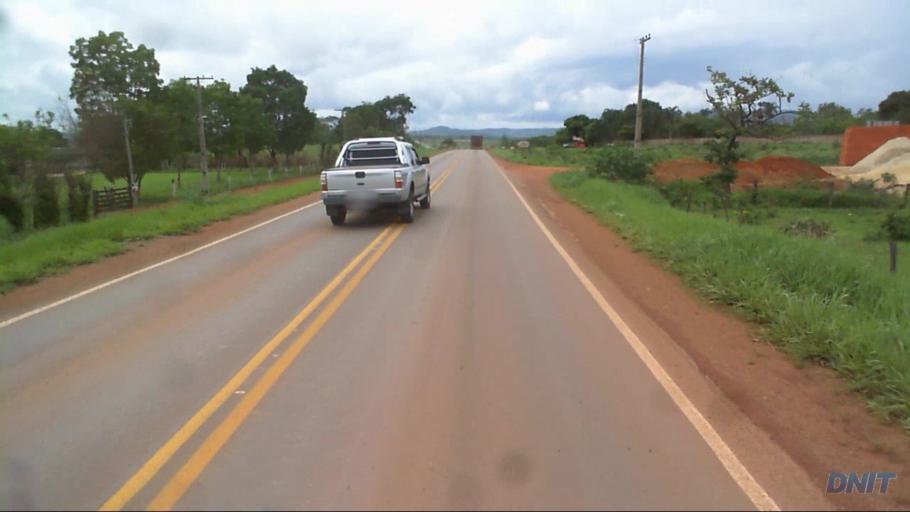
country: BR
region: Goias
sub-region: Padre Bernardo
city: Padre Bernardo
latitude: -15.3652
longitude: -48.2220
